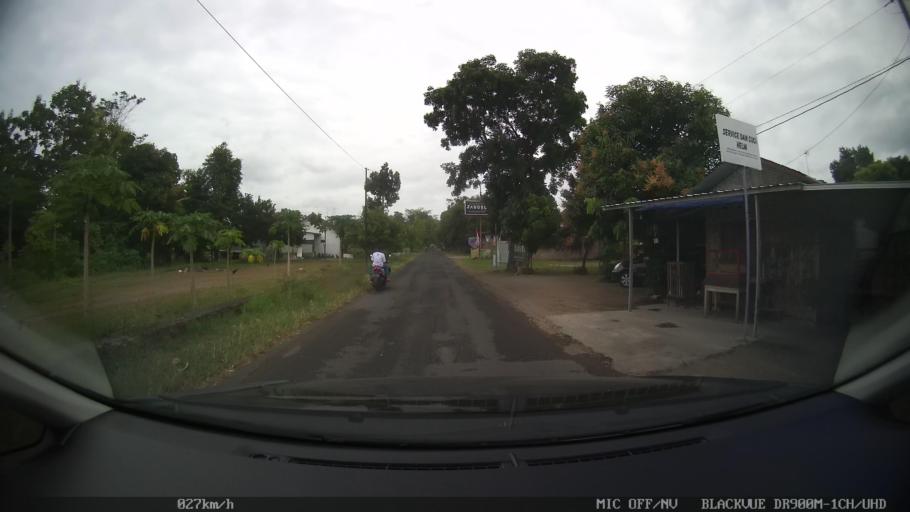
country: ID
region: Daerah Istimewa Yogyakarta
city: Sewon
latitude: -7.8605
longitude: 110.4011
